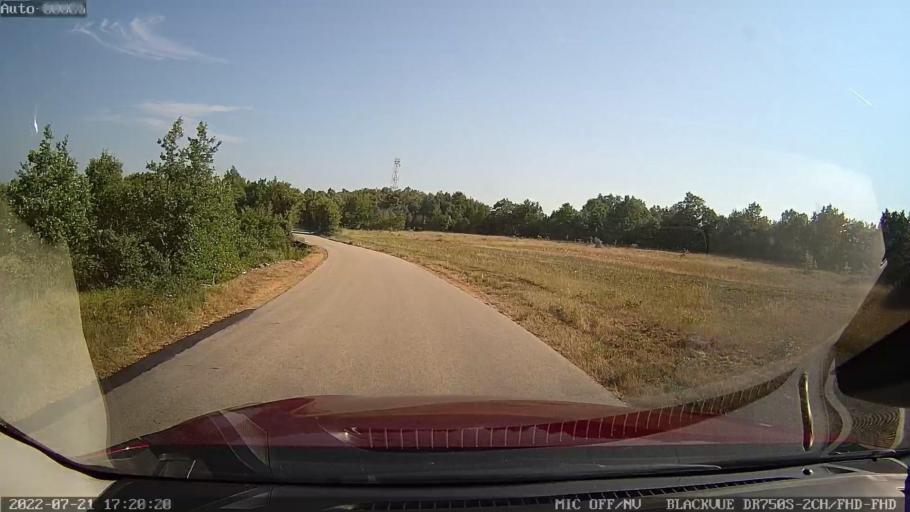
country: HR
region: Istarska
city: Karojba
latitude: 45.2047
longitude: 13.8283
